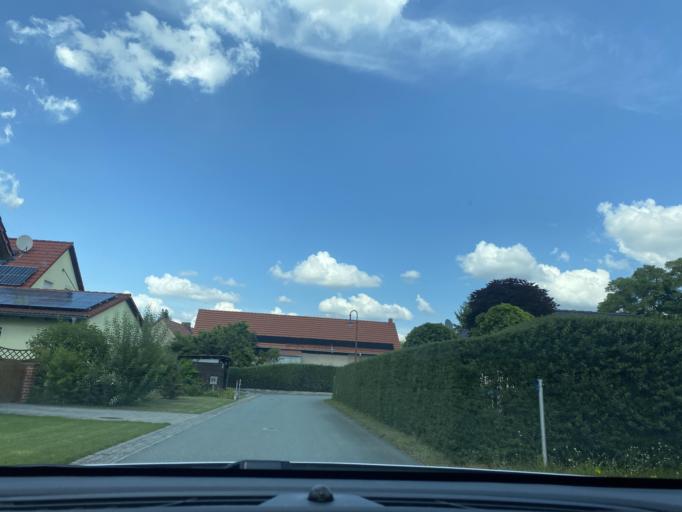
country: DE
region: Saxony
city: Boxberg
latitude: 51.4022
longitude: 14.5722
